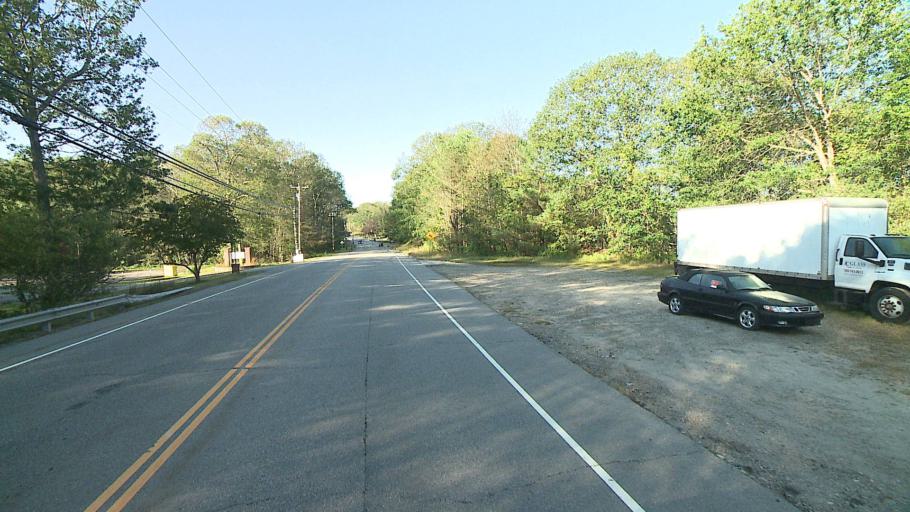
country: US
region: Connecticut
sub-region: Windham County
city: East Brooklyn
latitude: 41.7853
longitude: -71.8865
